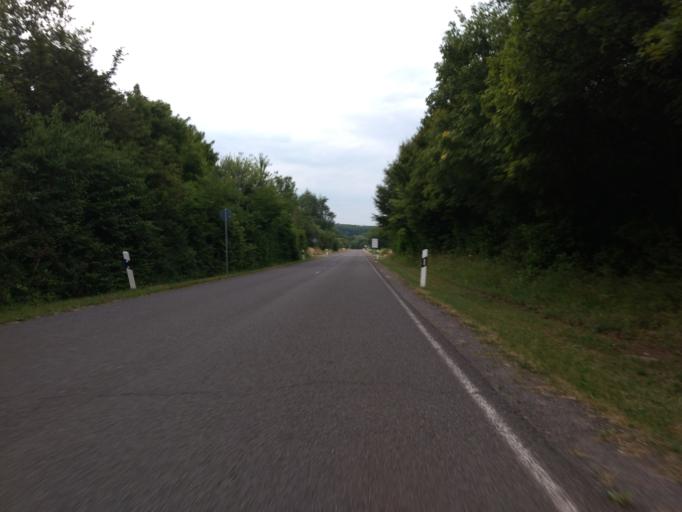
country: DE
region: Saarland
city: Rehlingen-Siersburg
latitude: 49.3279
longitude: 6.6685
